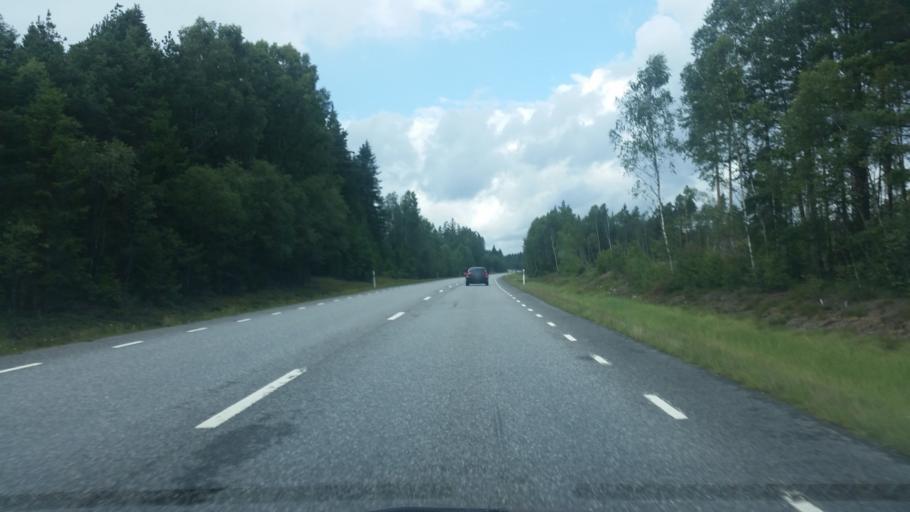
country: SE
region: Vaestra Goetaland
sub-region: Tranemo Kommun
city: Langhem
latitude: 57.5931
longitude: 13.1932
